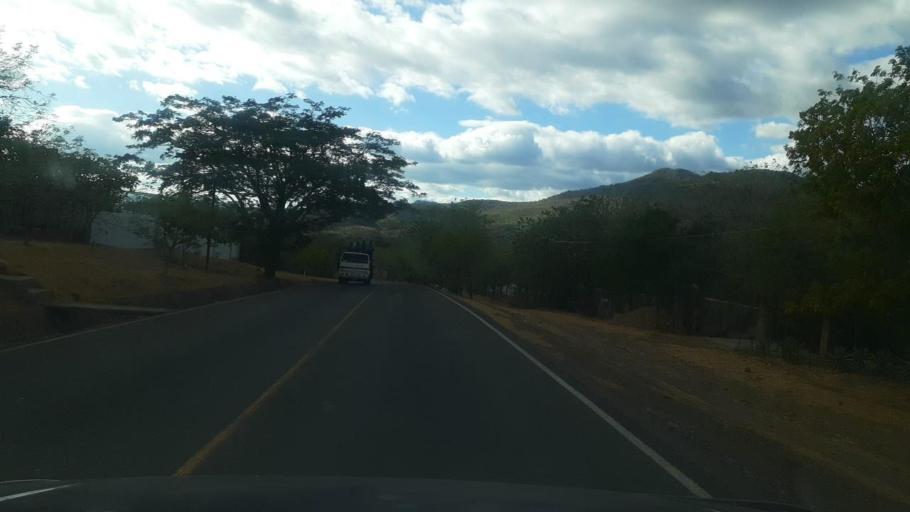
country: NI
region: Madriz
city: Somoto
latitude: 13.4718
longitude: -86.6115
